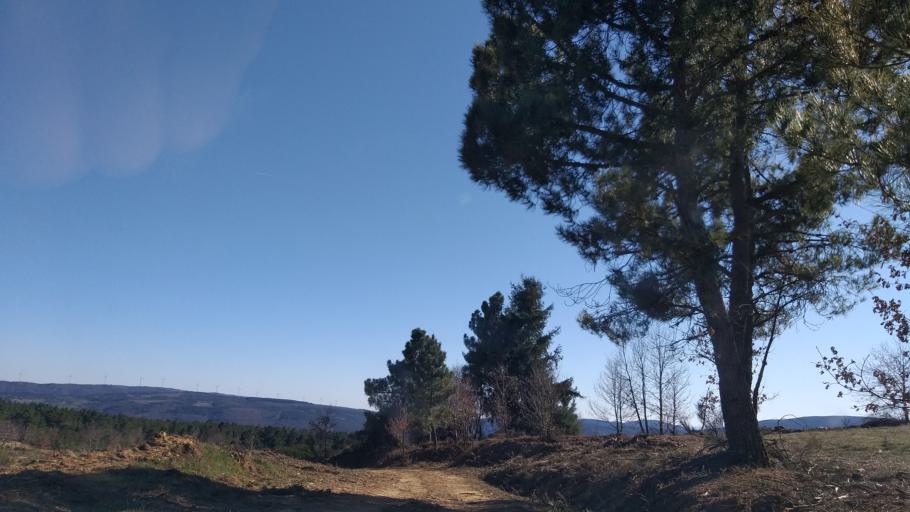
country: PT
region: Guarda
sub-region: Celorico da Beira
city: Celorico da Beira
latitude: 40.5170
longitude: -7.4121
